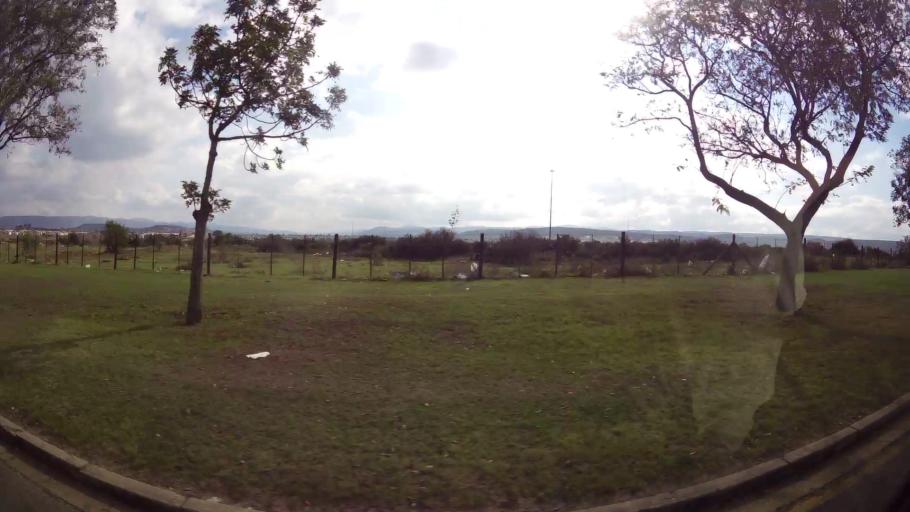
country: ZA
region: Eastern Cape
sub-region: Nelson Mandela Bay Metropolitan Municipality
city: Uitenhage
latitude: -33.7457
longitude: 25.4018
